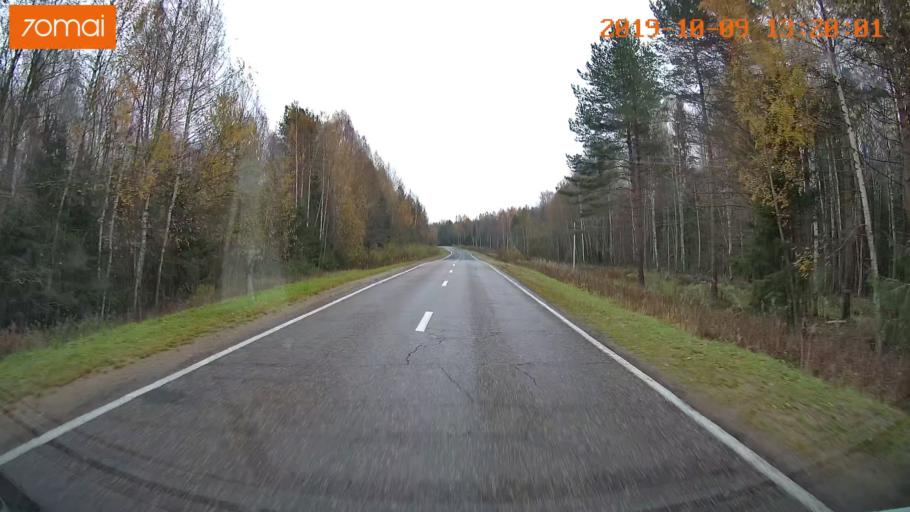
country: RU
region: Jaroslavl
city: Lyubim
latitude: 58.3457
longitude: 40.8241
